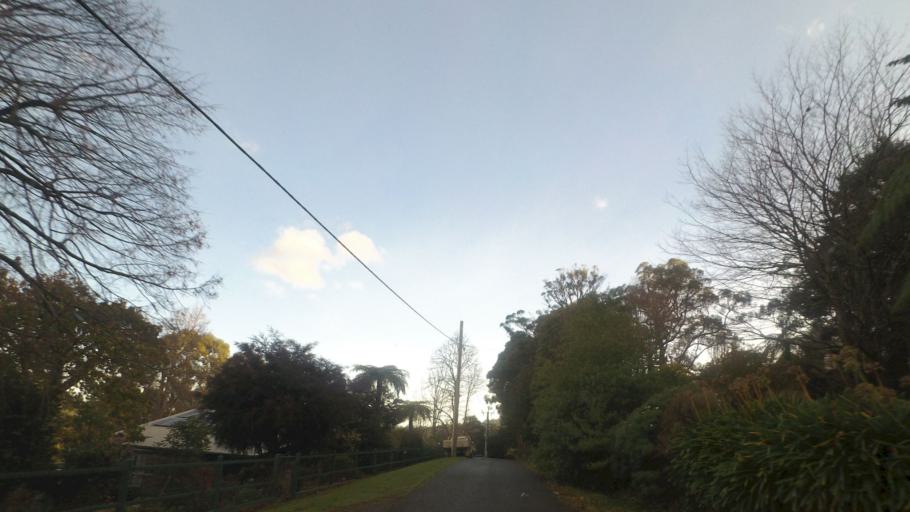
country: AU
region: Victoria
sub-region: Yarra Ranges
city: Kalorama
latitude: -37.8160
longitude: 145.3758
